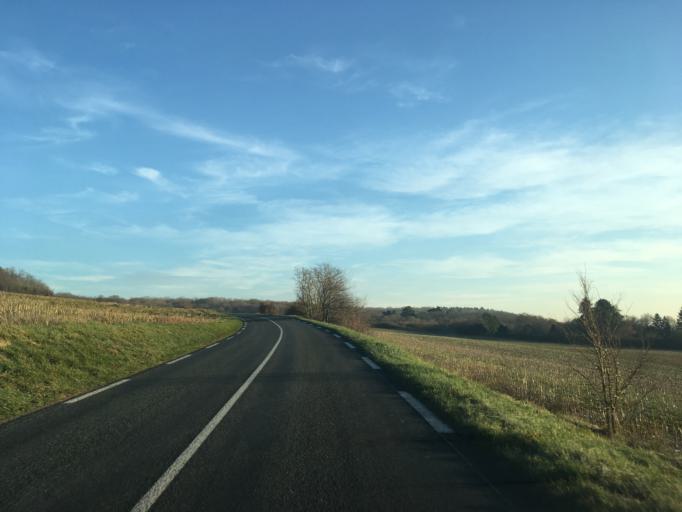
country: FR
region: Haute-Normandie
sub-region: Departement de l'Eure
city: Houlbec-Cocherel
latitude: 49.0556
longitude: 1.3395
